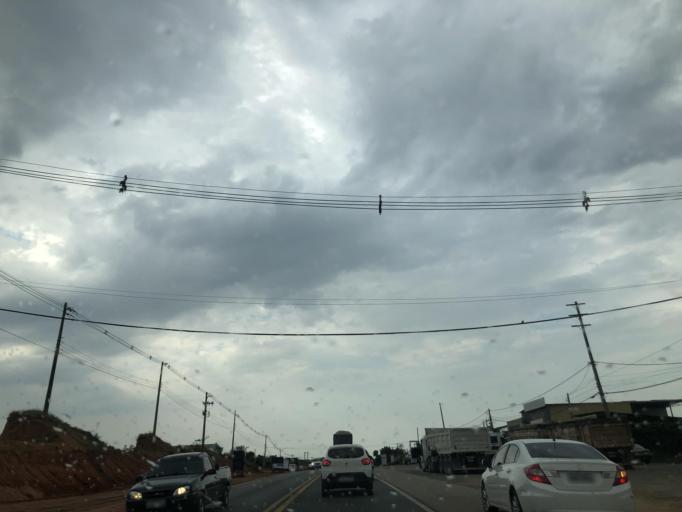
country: BR
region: Sao Paulo
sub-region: Salto De Pirapora
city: Salto de Pirapora
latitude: -23.6460
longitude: -47.5834
